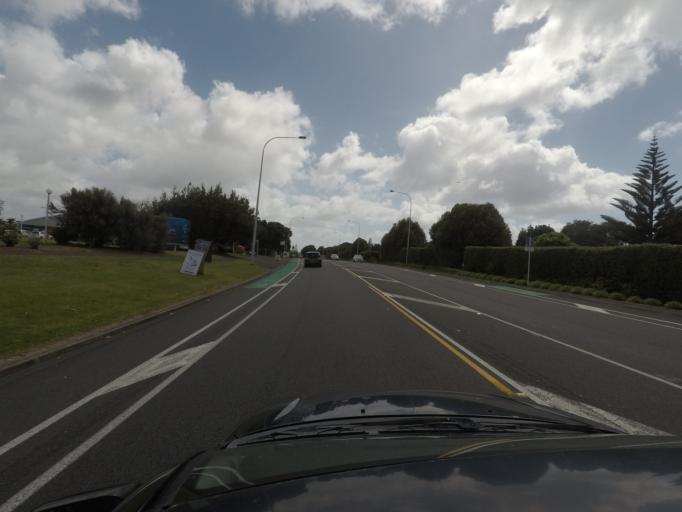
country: NZ
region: Auckland
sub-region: Auckland
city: Rothesay Bay
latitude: -36.5985
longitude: 174.6983
